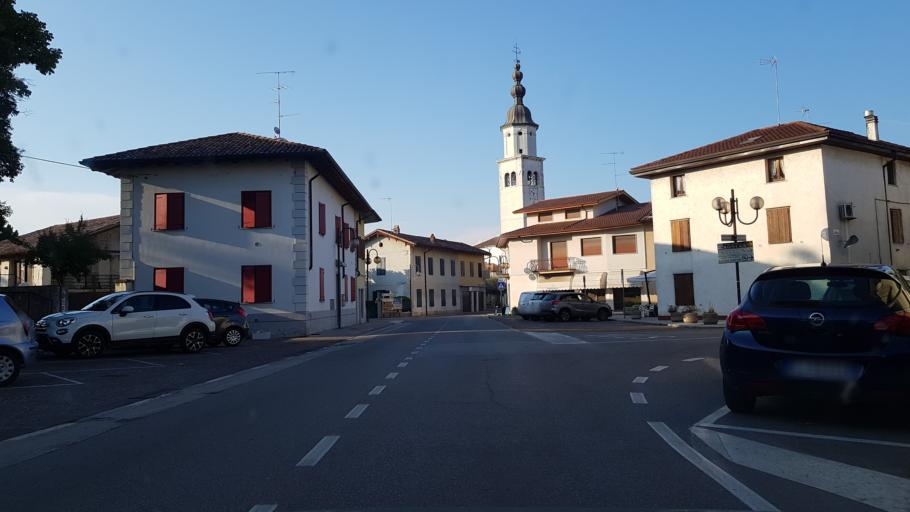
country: IT
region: Friuli Venezia Giulia
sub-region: Provincia di Gorizia
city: Capriva del Friuli
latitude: 45.9415
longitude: 13.5144
